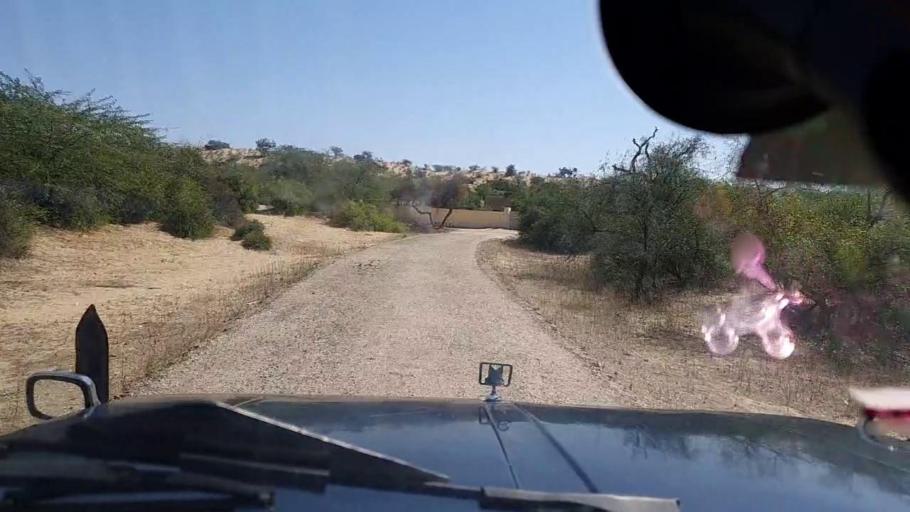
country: PK
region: Sindh
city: Mithi
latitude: 24.5954
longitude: 69.7143
